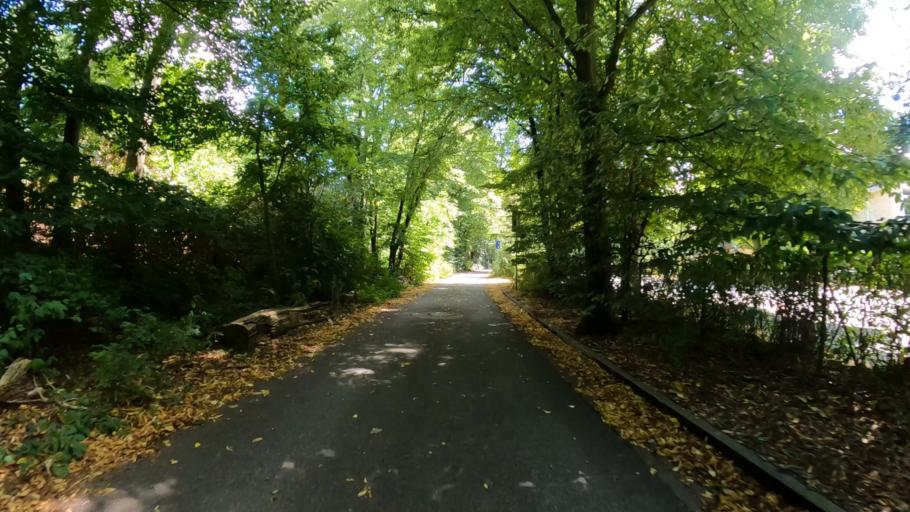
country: DE
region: Hamburg
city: Ohlsdorf
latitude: 53.6286
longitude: 10.0323
